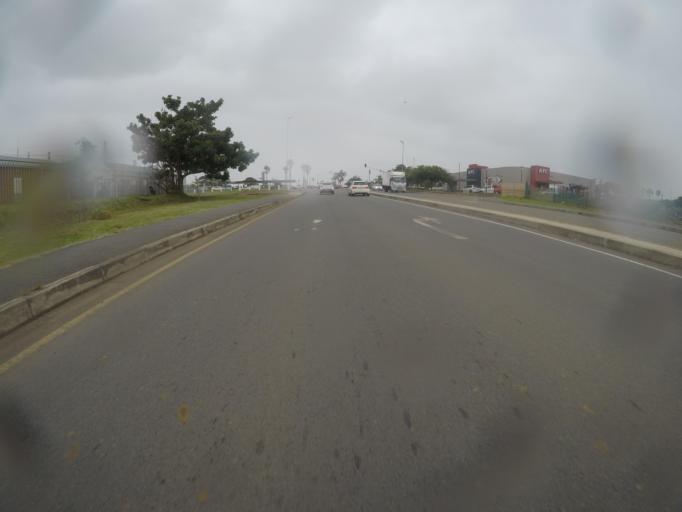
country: ZA
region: Eastern Cape
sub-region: Buffalo City Metropolitan Municipality
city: East London
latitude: -32.9359
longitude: 27.9931
